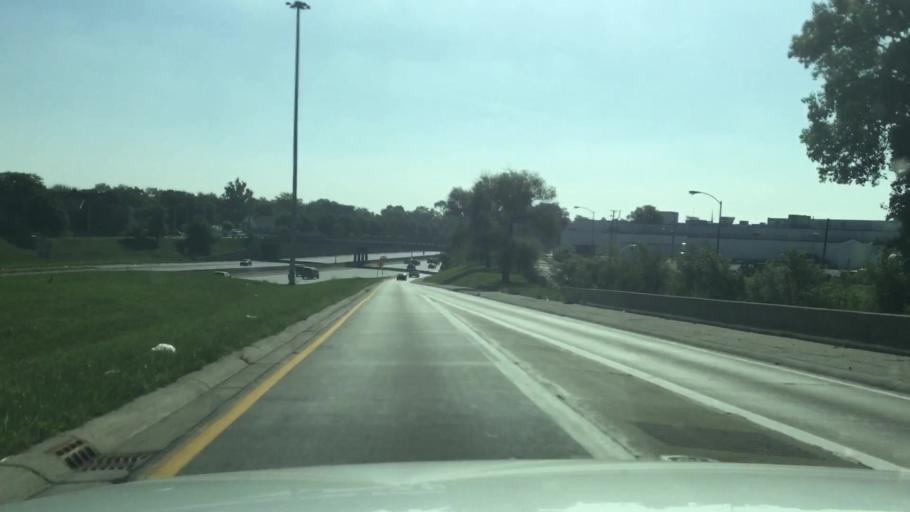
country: US
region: Michigan
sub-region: Wayne County
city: Highland Park
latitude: 42.4070
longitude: -83.0785
